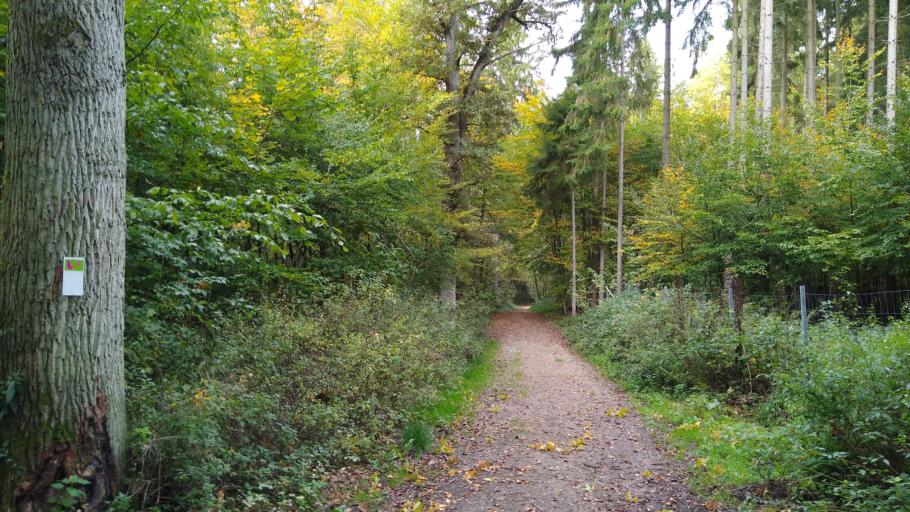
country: DE
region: Bavaria
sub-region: Regierungsbezirk Mittelfranken
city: Obermichelbach
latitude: 49.5049
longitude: 10.9240
